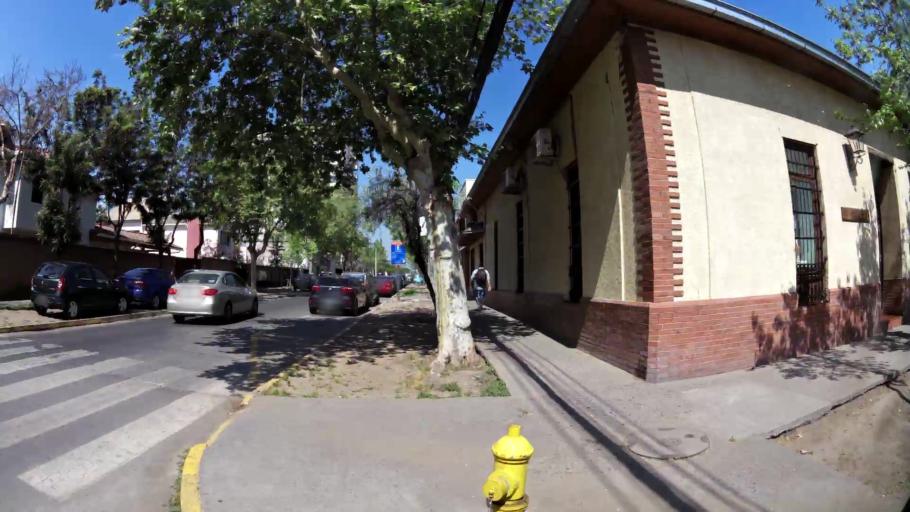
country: CL
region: Santiago Metropolitan
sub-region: Provincia de Maipo
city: San Bernardo
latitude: -33.5925
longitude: -70.7010
